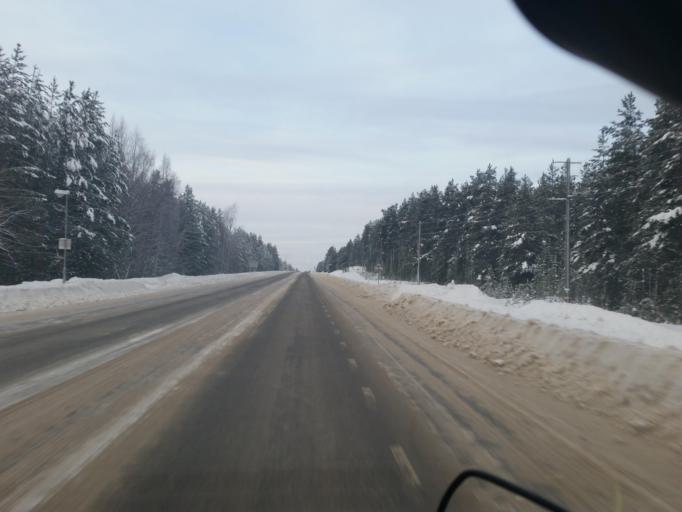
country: SE
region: Norrbotten
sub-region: Pitea Kommun
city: Pitea
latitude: 65.2707
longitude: 21.5284
